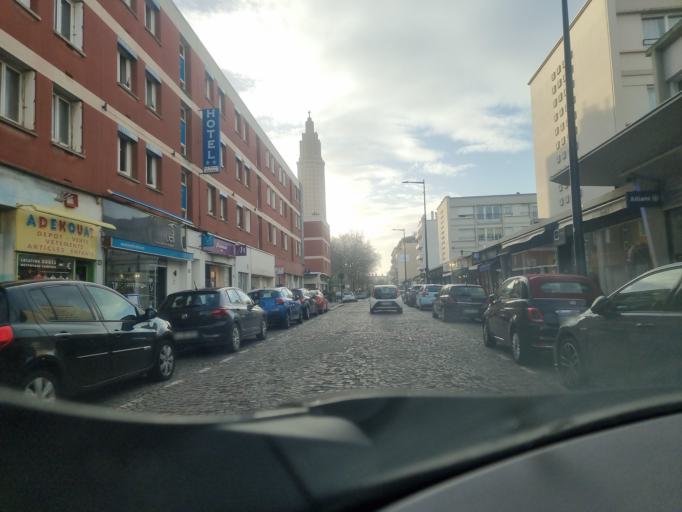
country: FR
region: Haute-Normandie
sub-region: Departement de la Seine-Maritime
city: Le Havre
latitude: 49.4912
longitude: 0.1048
